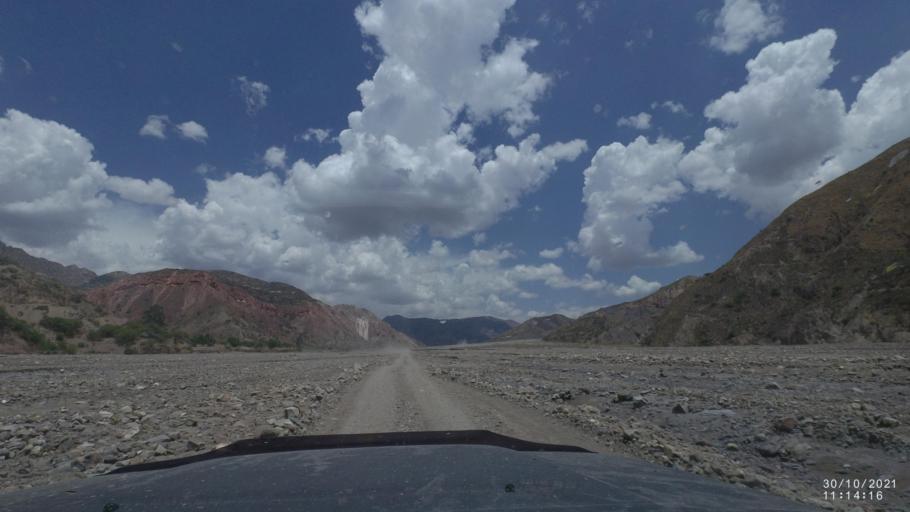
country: BO
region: Cochabamba
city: Sipe Sipe
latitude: -17.5266
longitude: -66.5815
